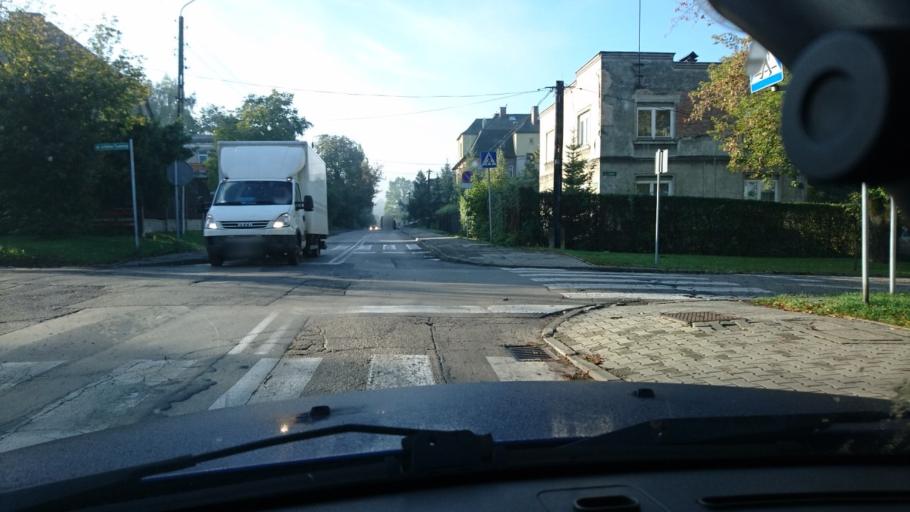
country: PL
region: Silesian Voivodeship
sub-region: Bielsko-Biala
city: Bielsko-Biala
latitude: 49.8136
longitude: 19.0585
